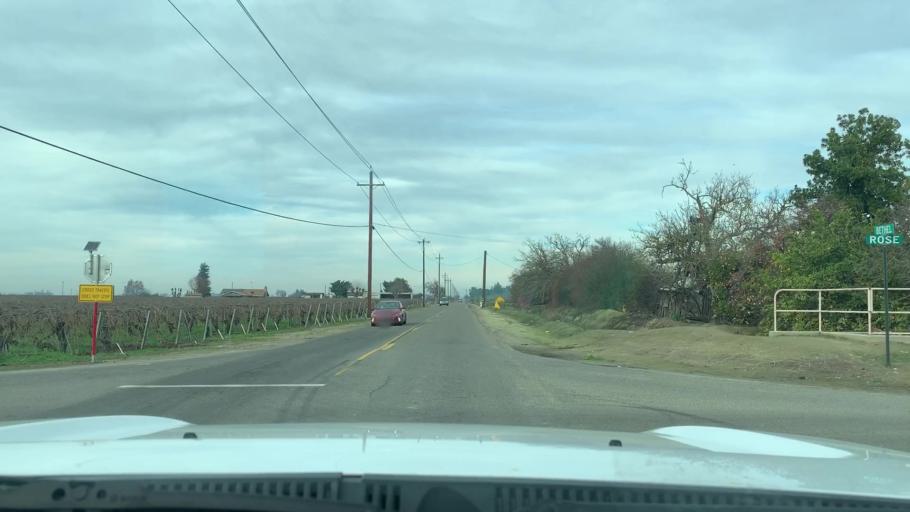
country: US
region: California
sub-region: Fresno County
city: Selma
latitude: 36.5687
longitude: -119.5750
